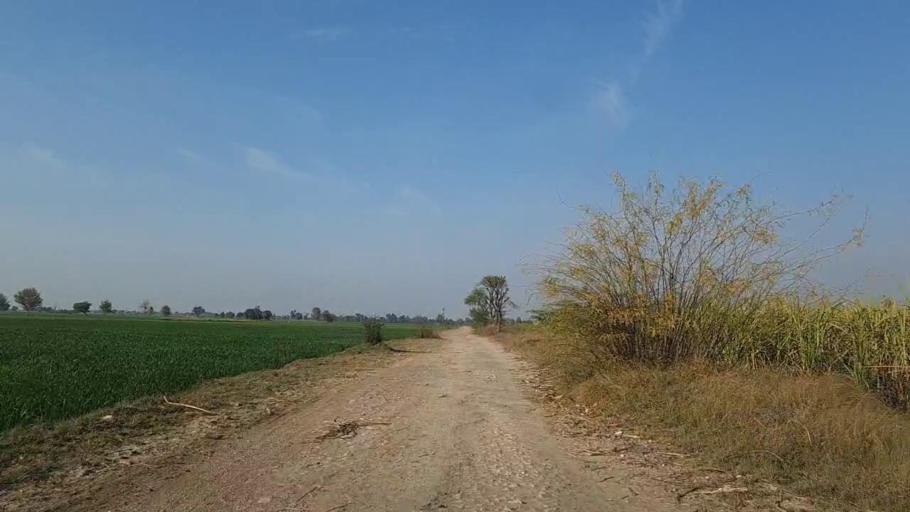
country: PK
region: Sindh
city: Nawabshah
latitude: 26.3705
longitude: 68.4848
